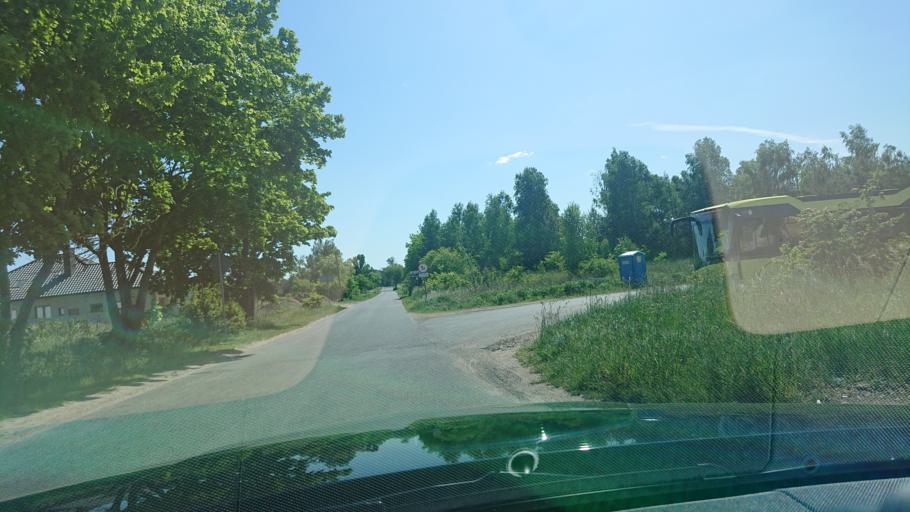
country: PL
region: Greater Poland Voivodeship
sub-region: Powiat gnieznienski
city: Gniezno
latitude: 52.5014
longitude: 17.5843
